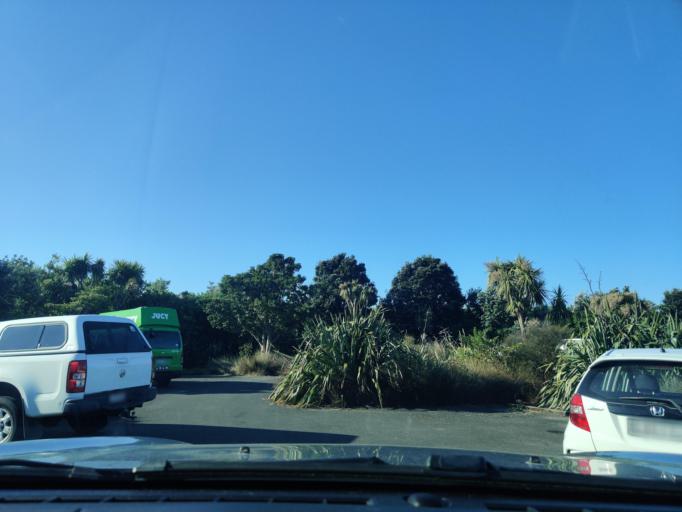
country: NZ
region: Taranaki
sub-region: New Plymouth District
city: New Plymouth
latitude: -39.0385
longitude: 174.1134
